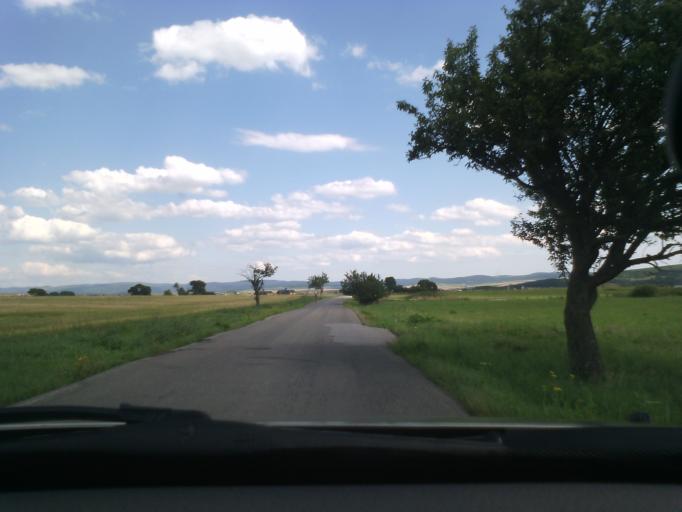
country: SK
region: Presovsky
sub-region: Okres Poprad
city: Nova Lesna
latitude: 49.1279
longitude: 20.3266
